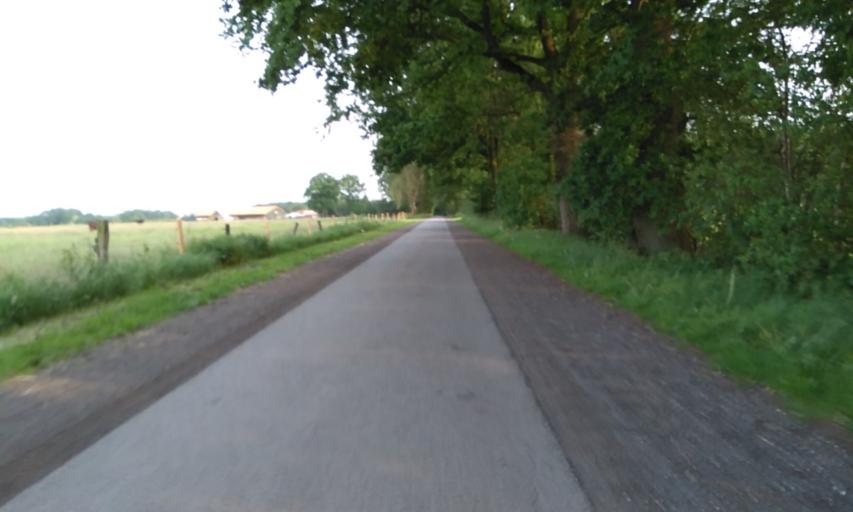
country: DE
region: Lower Saxony
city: Bargstedt
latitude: 53.4897
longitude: 9.4632
